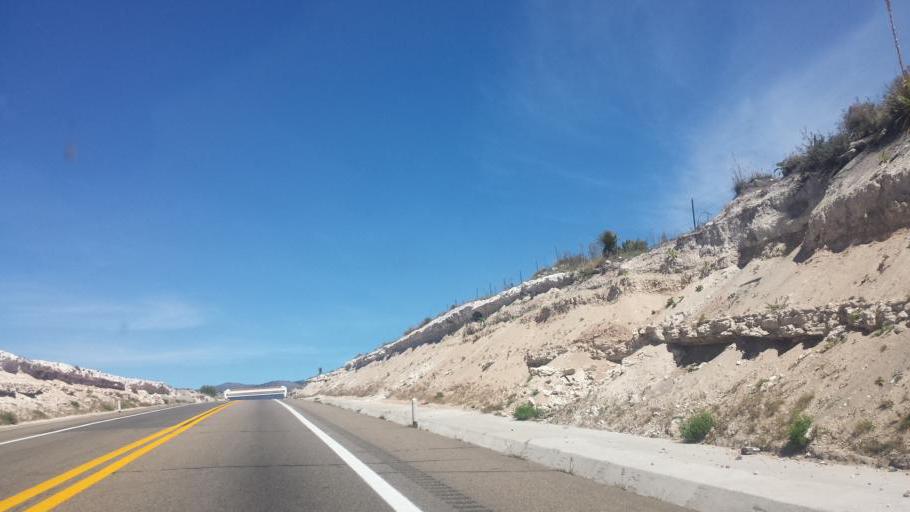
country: MX
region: Oaxaca
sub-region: Villa Tejupam de la Union
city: Villa Tejupam de la Union
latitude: 17.9143
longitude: -97.3624
